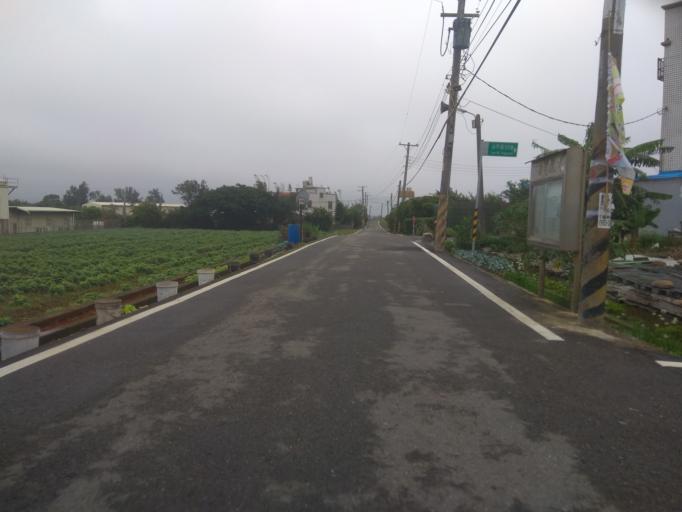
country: TW
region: Taiwan
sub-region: Hsinchu
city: Zhubei
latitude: 24.9911
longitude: 121.0368
